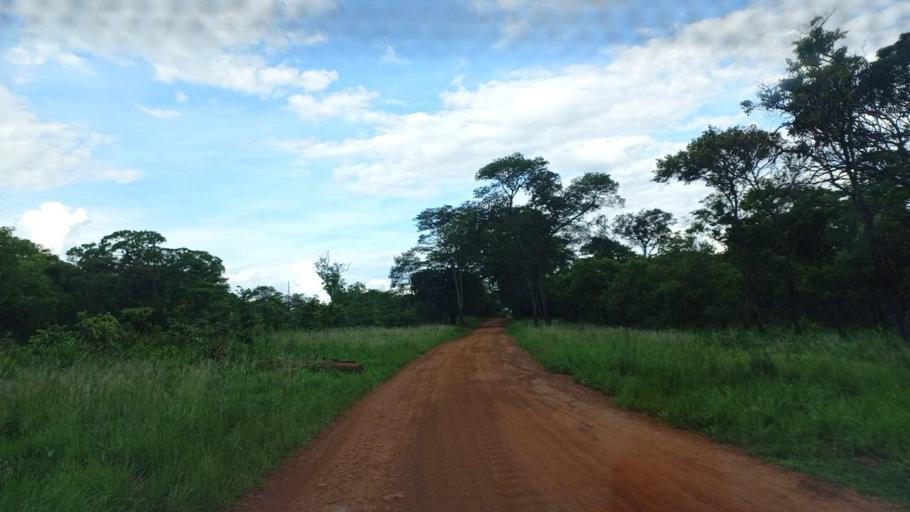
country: ZM
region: North-Western
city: Mwinilunga
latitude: -11.7816
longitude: 24.3741
